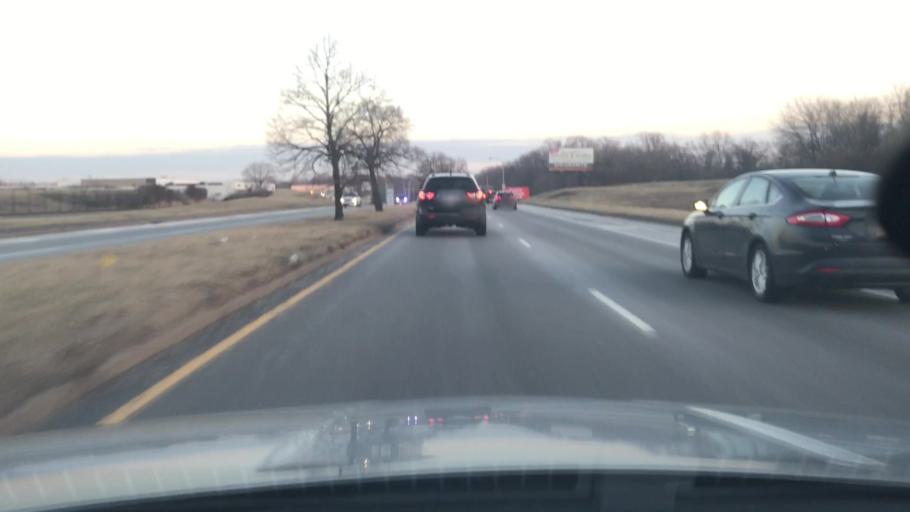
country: US
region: New Jersey
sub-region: Burlington County
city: Riverton
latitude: 40.0767
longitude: -75.0205
